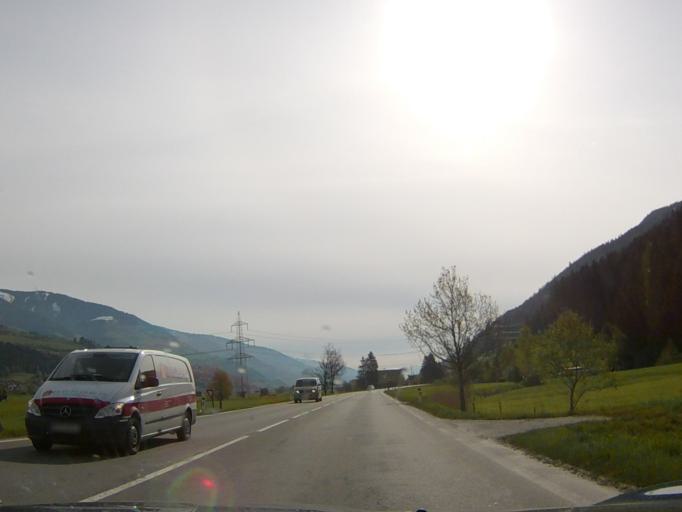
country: AT
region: Salzburg
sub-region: Politischer Bezirk Zell am See
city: Hollersbach im Pinzgau
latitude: 47.2773
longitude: 12.4232
